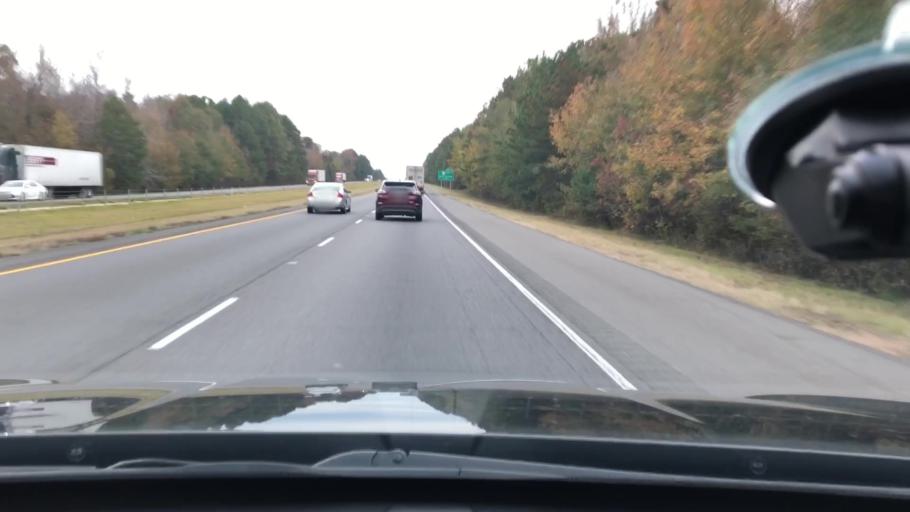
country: US
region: Arkansas
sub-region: Clark County
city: Arkadelphia
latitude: 34.0540
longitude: -93.1320
